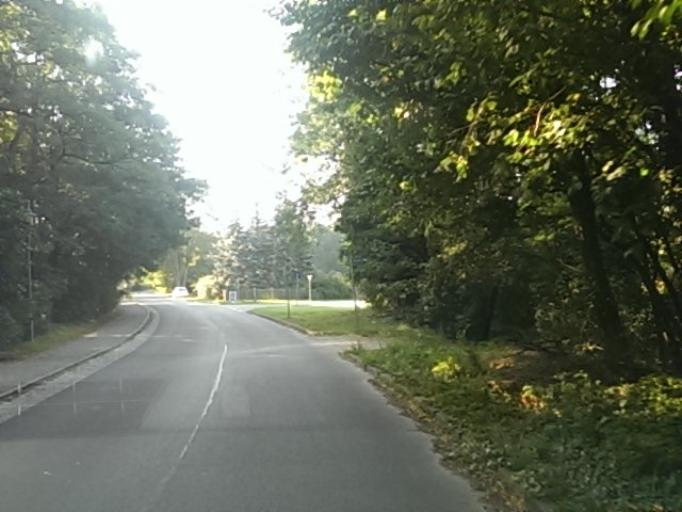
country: DE
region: Brandenburg
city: Trebbin
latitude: 52.2097
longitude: 13.1472
